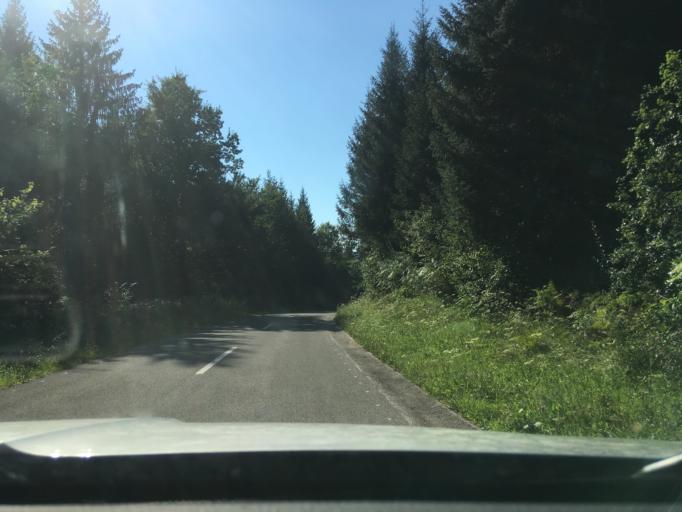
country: SI
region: Crnomelj
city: Crnomelj
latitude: 45.4571
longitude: 15.2292
